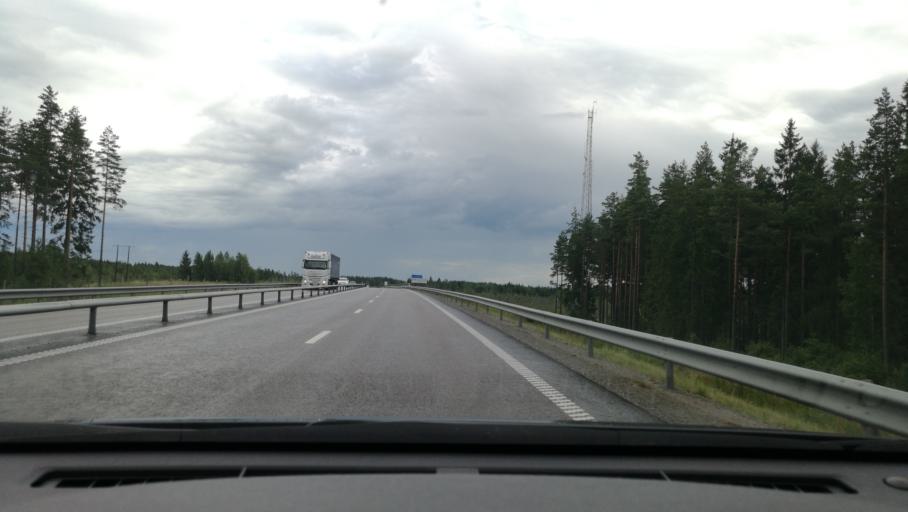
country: SE
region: Soedermanland
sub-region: Katrineholms Kommun
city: Katrineholm
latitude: 59.0020
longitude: 16.2479
